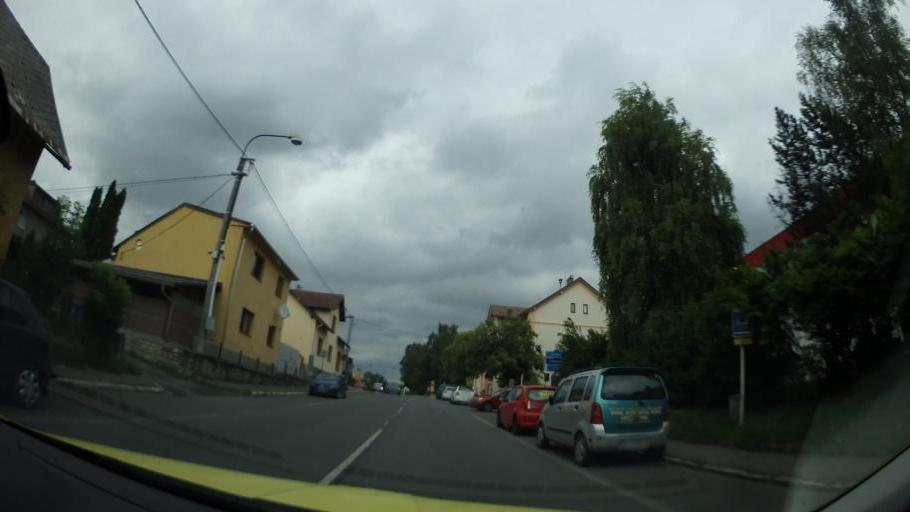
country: CZ
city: Stramberk
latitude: 49.5830
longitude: 18.1294
